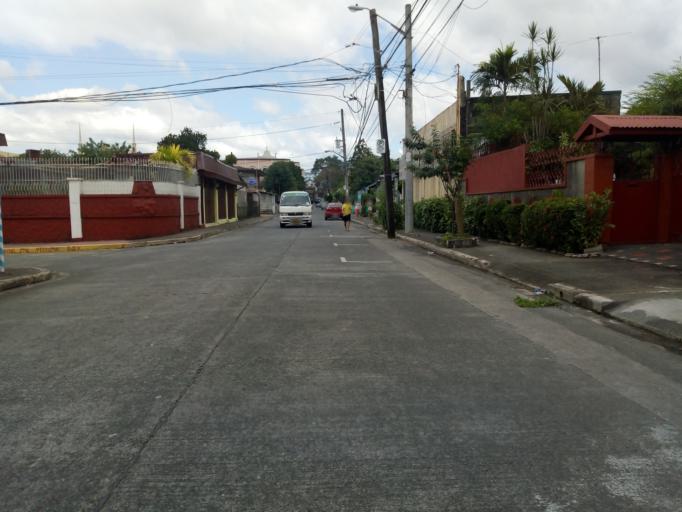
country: PH
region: Calabarzon
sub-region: Province of Rizal
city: Antipolo
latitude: 14.6378
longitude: 121.1205
